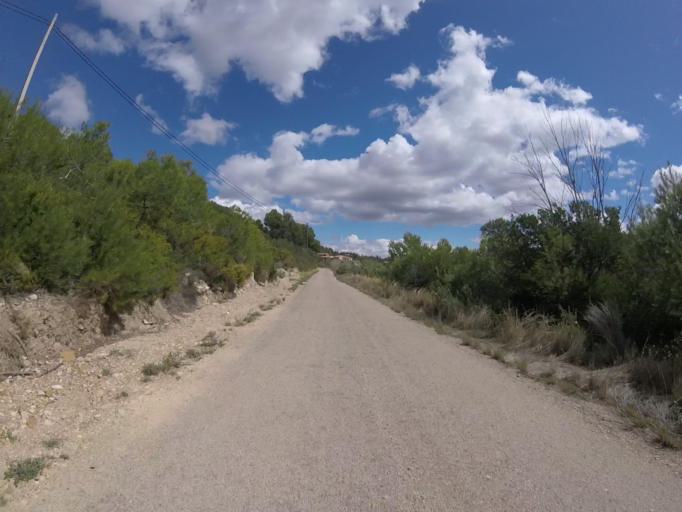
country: ES
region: Valencia
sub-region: Provincia de Castello
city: Sierra-Engarceran
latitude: 40.2780
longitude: -0.0780
